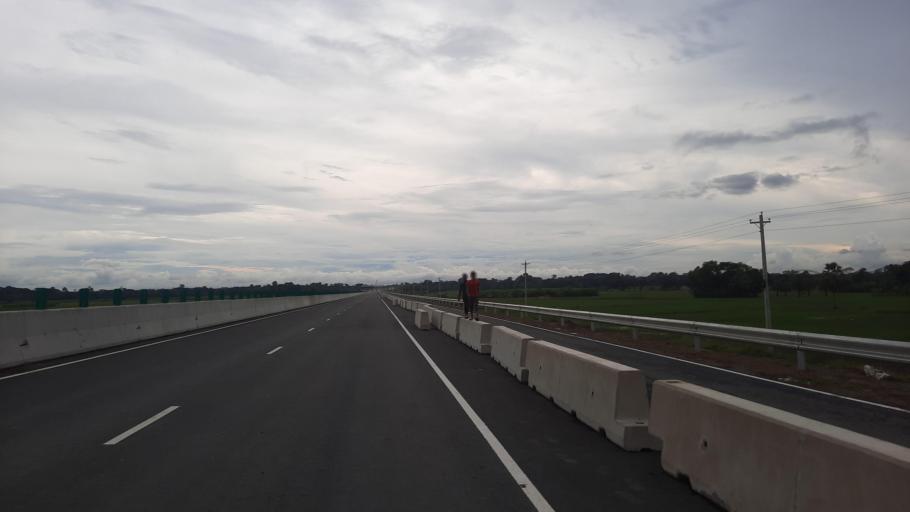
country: BD
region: Khulna
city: Kalia
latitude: 23.2035
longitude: 89.7086
